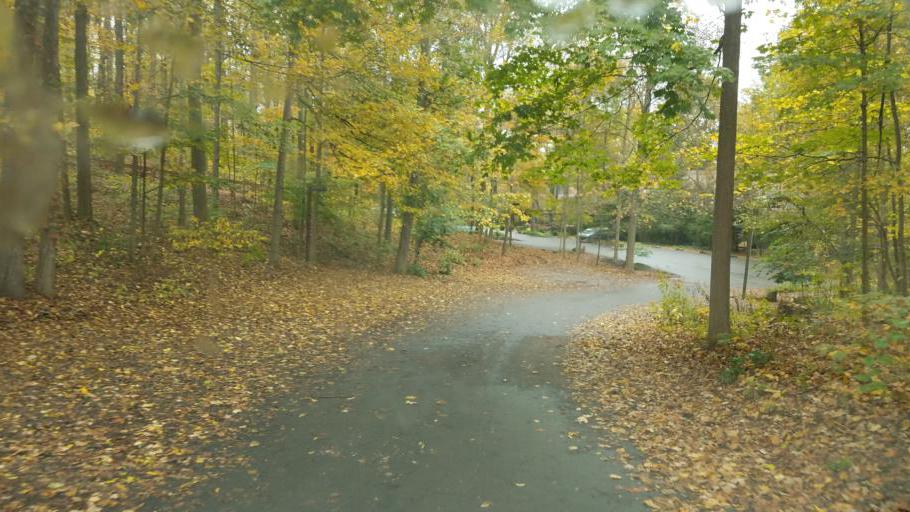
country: US
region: Ohio
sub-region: Holmes County
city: Millersburg
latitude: 40.5728
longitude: -81.8732
